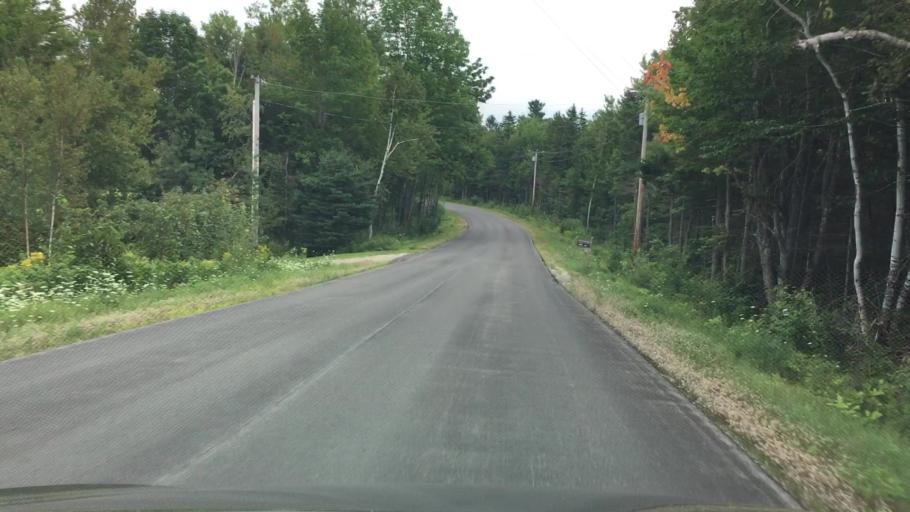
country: US
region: Maine
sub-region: Waldo County
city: Stockton Springs
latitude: 44.5260
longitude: -68.8772
